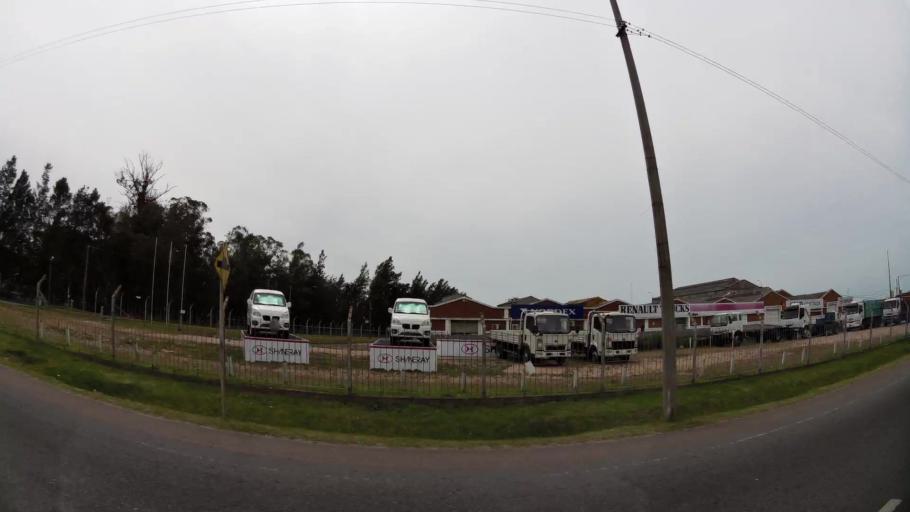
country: UY
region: Canelones
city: La Paz
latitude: -34.7888
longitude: -56.2241
